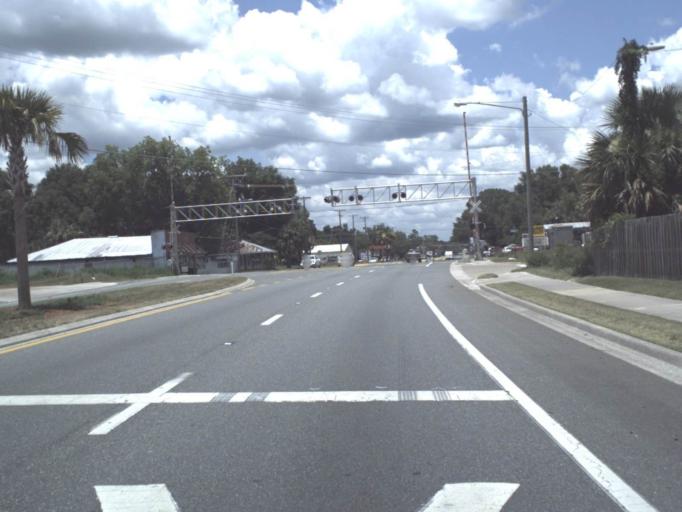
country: US
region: Florida
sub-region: Taylor County
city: Perry
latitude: 30.1060
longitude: -83.5891
